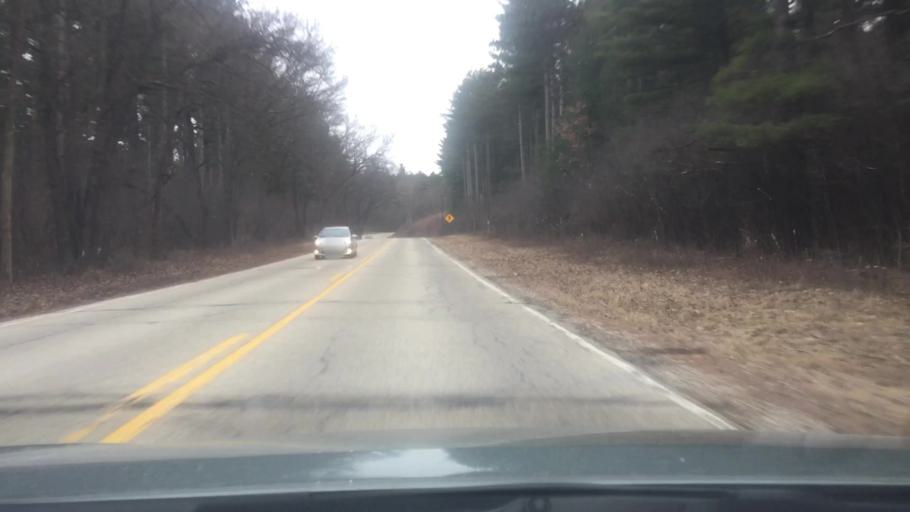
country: US
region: Wisconsin
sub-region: Waukesha County
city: North Prairie
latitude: 42.9404
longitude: -88.4601
